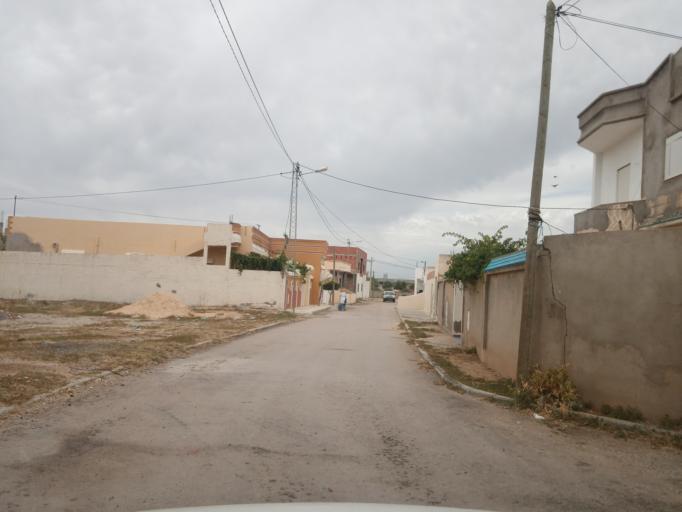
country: TN
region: Al Qayrawan
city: Sbikha
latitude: 36.1155
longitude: 10.0919
